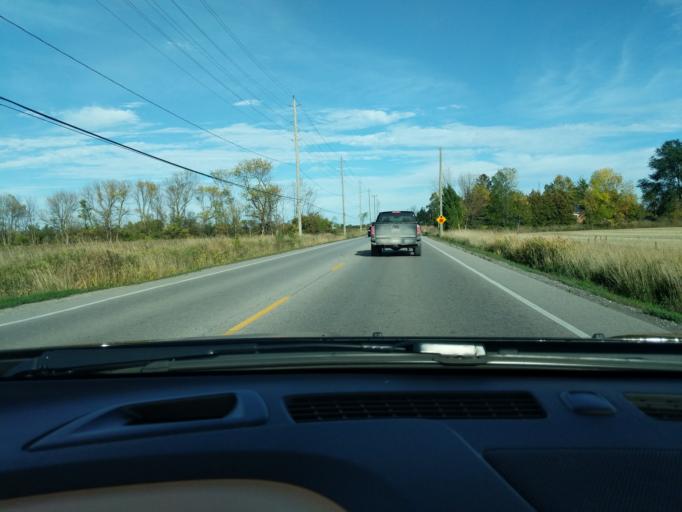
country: CA
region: Ontario
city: Collingwood
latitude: 44.4853
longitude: -80.1826
